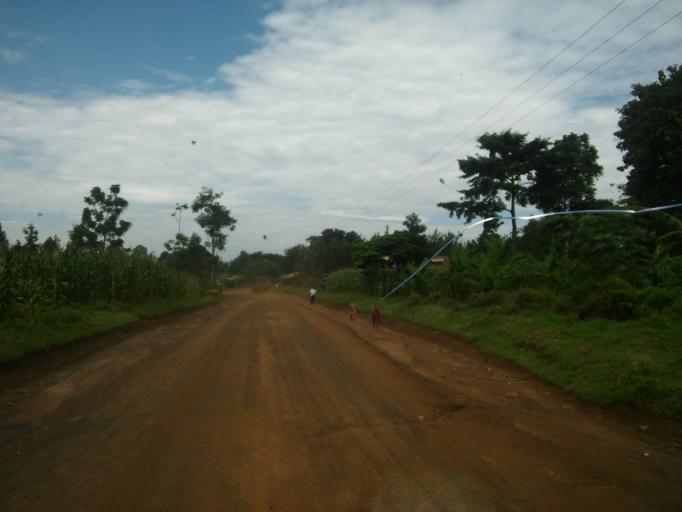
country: KE
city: Malikisi
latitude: 0.8122
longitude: 34.3330
